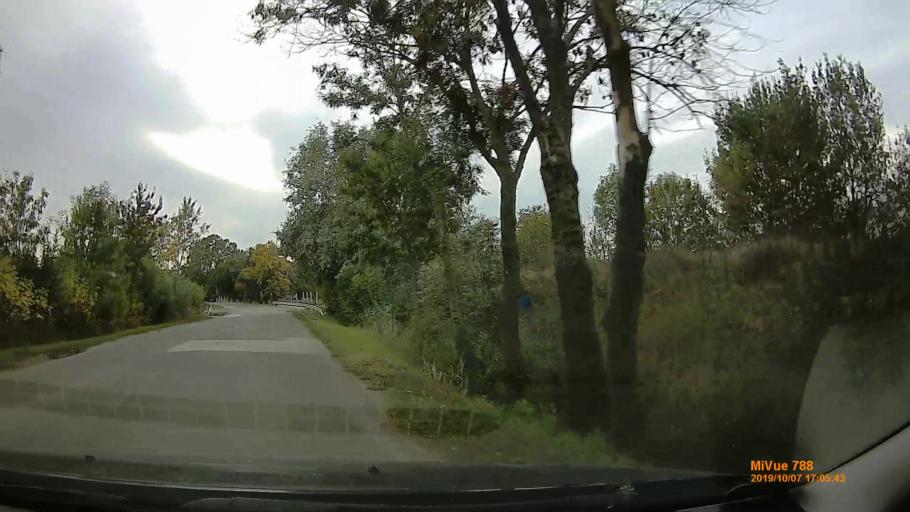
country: HU
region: Bekes
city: Szarvas
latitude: 46.8243
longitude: 20.5340
